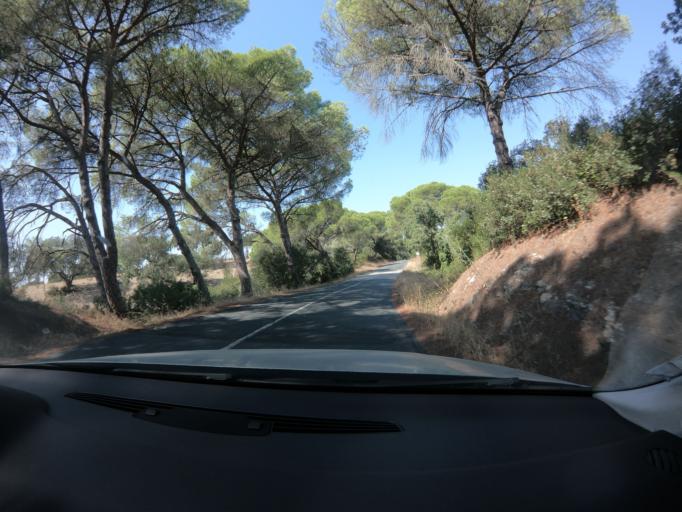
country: PT
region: Setubal
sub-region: Alcacer do Sal
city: Alcacer do Sal
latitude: 38.3039
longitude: -8.4177
